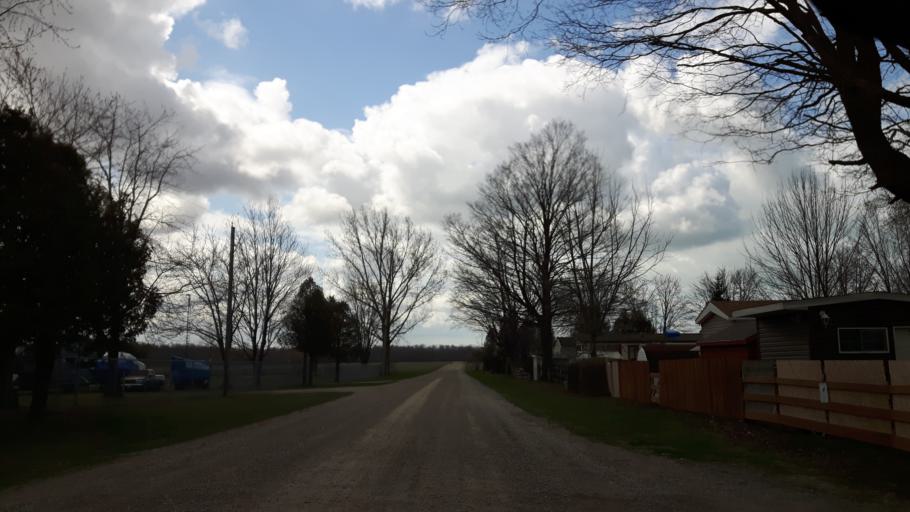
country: CA
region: Ontario
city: Bluewater
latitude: 43.5486
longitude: -81.7008
